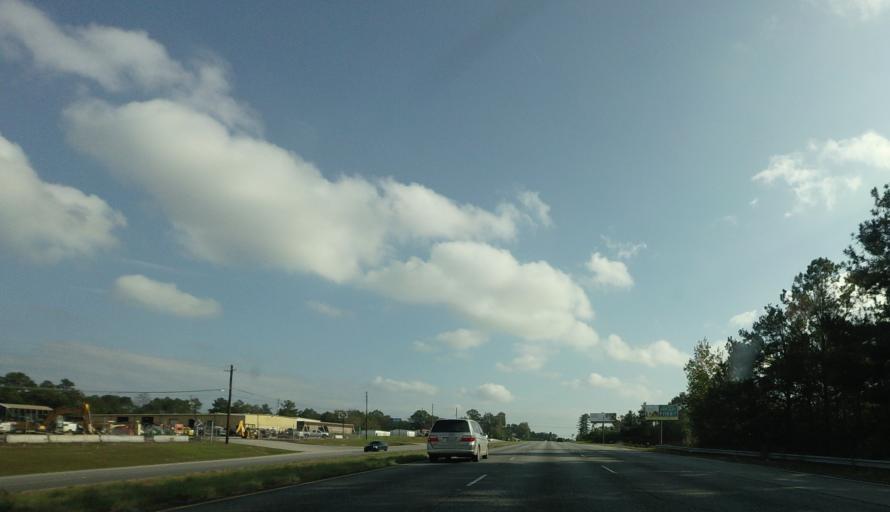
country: US
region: Georgia
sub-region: Bibb County
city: Macon
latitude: 32.7552
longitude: -83.6608
